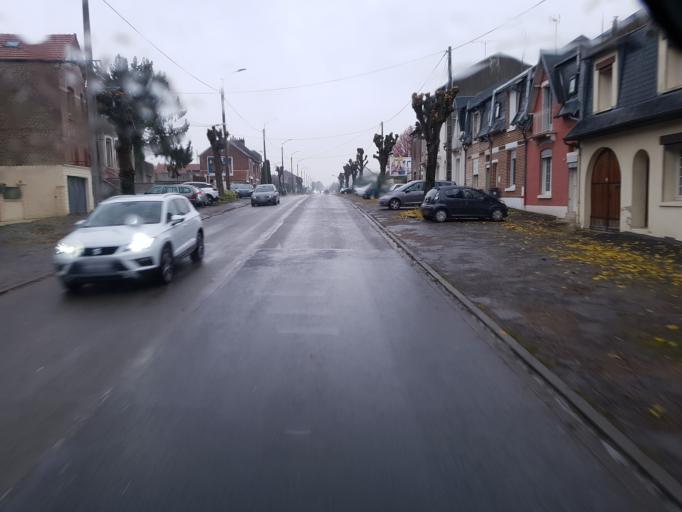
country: FR
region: Picardie
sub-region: Departement de l'Aisne
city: Saint-Quentin
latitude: 49.8623
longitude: 3.2758
